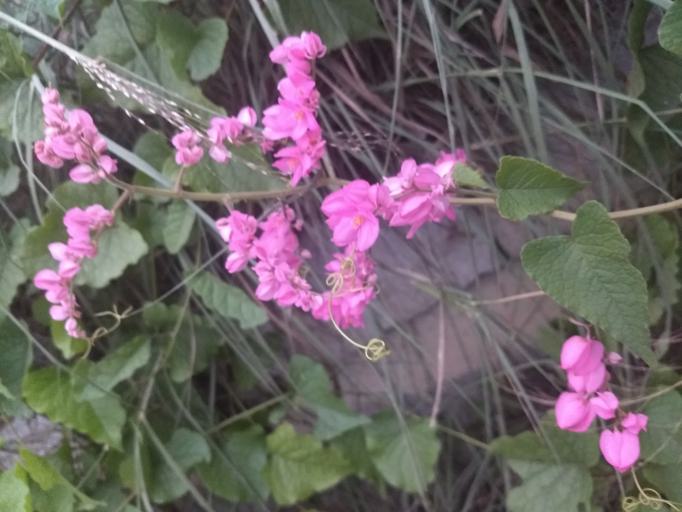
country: MX
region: Nuevo Leon
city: Santiago
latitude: 25.3927
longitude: -100.1409
